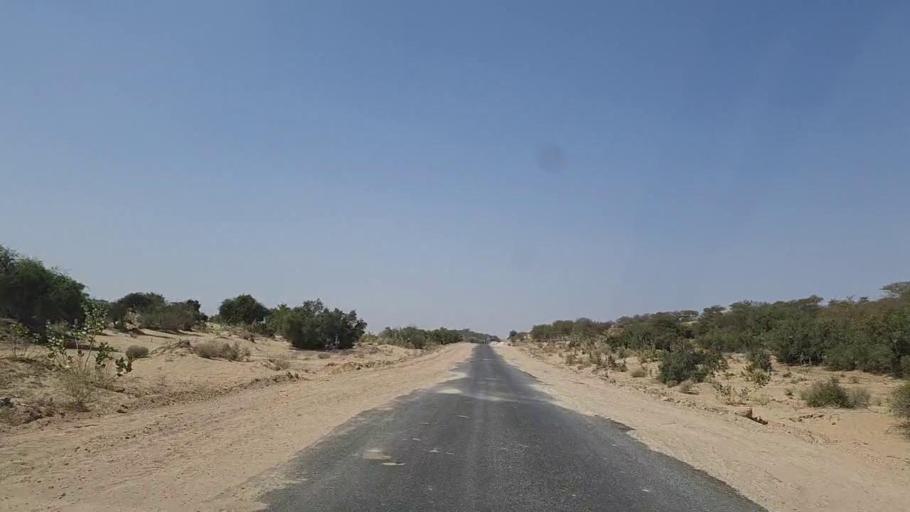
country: PK
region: Sindh
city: Diplo
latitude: 24.5876
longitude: 69.5408
